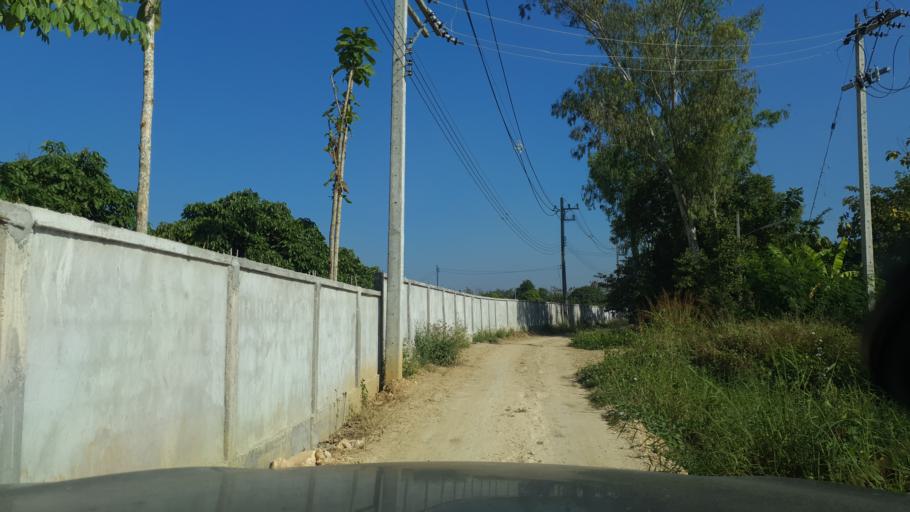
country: TH
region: Chiang Mai
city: Saraphi
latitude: 18.7192
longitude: 99.0754
